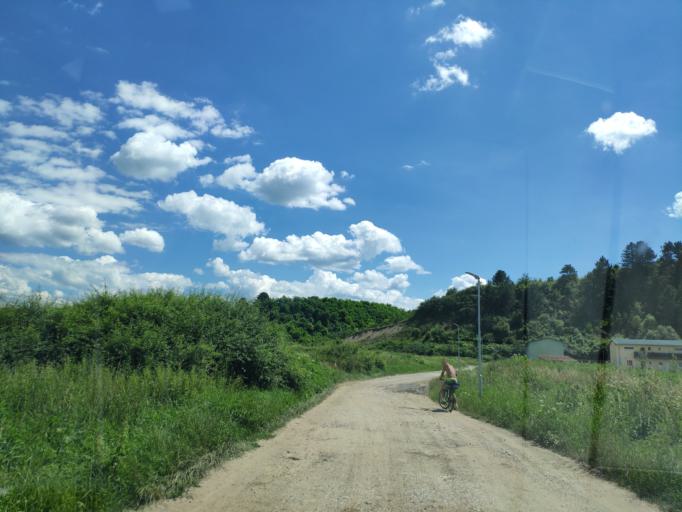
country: HU
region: Borsod-Abauj-Zemplen
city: Arlo
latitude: 48.2782
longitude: 20.1923
